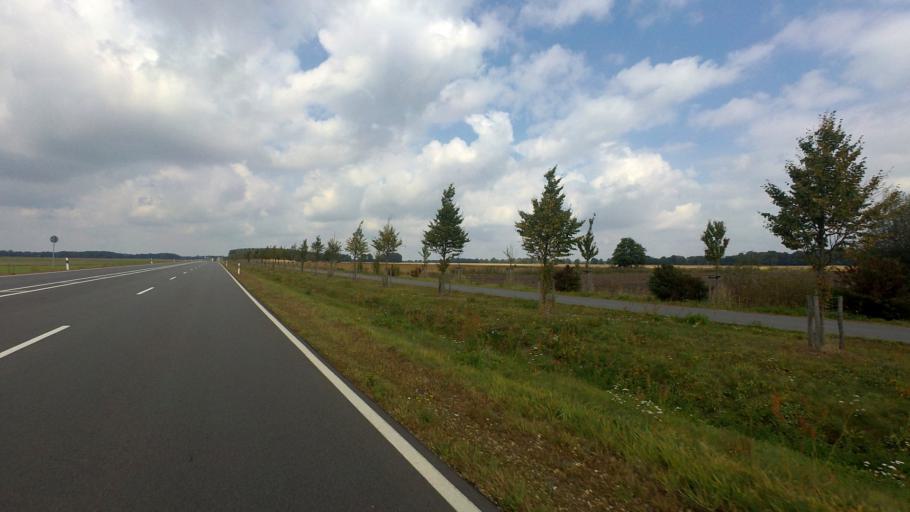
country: DE
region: Brandenburg
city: Herzberg
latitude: 51.6625
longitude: 13.2808
